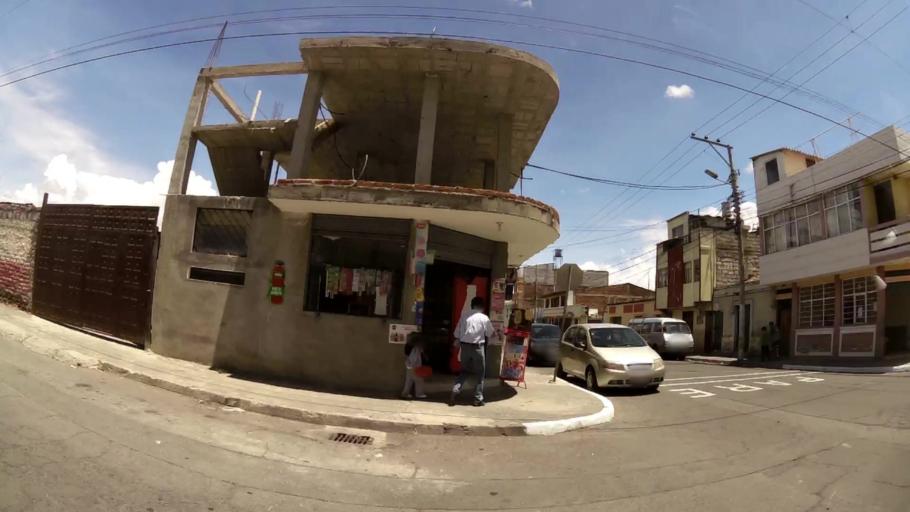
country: EC
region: Chimborazo
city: Riobamba
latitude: -1.6782
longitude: -78.6562
